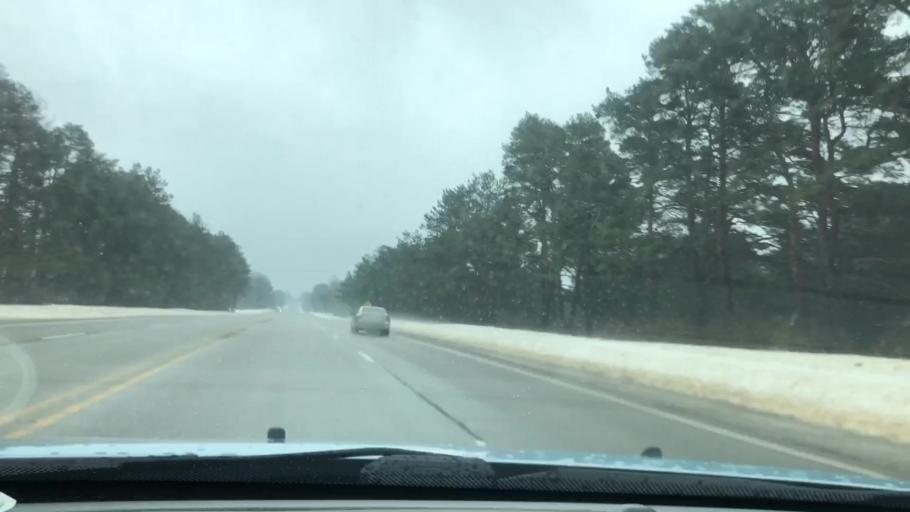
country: US
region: Michigan
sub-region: Otsego County
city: Gaylord
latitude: 45.0621
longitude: -84.8340
